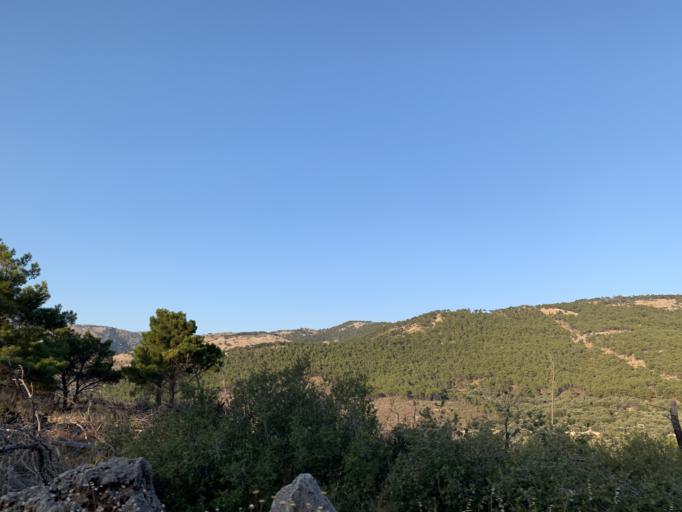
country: GR
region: North Aegean
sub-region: Chios
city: Chios
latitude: 38.3792
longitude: 26.0192
